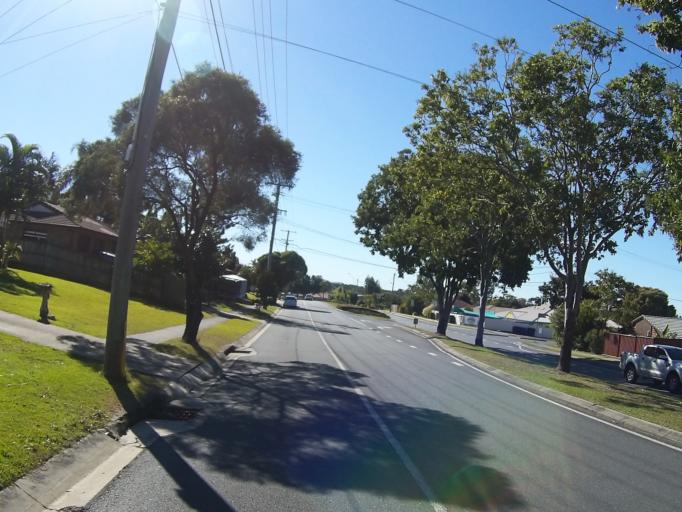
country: AU
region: Queensland
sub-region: Logan
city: Windaroo
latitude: -27.7324
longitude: 153.2080
